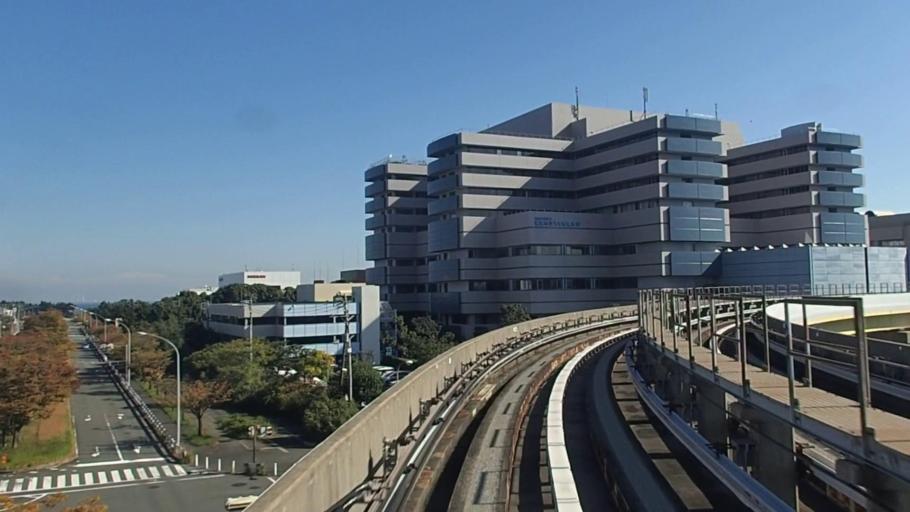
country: JP
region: Kanagawa
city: Yokosuka
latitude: 35.3456
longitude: 139.6496
